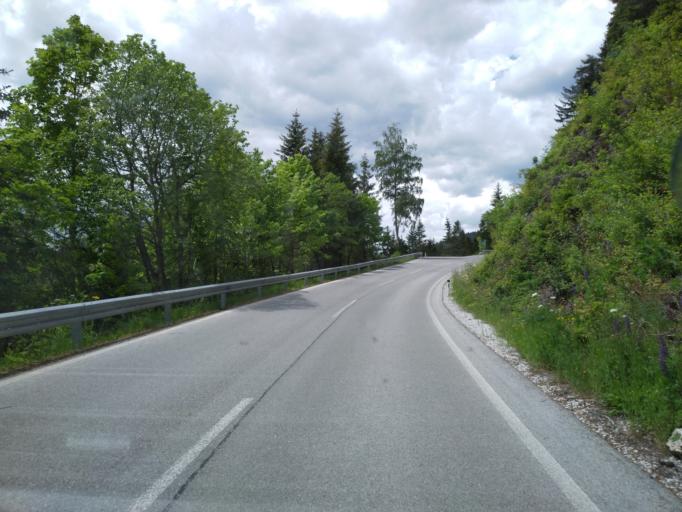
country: AT
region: Salzburg
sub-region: Politischer Bezirk Sankt Johann im Pongau
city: Filzmoos
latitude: 47.4283
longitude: 13.5859
